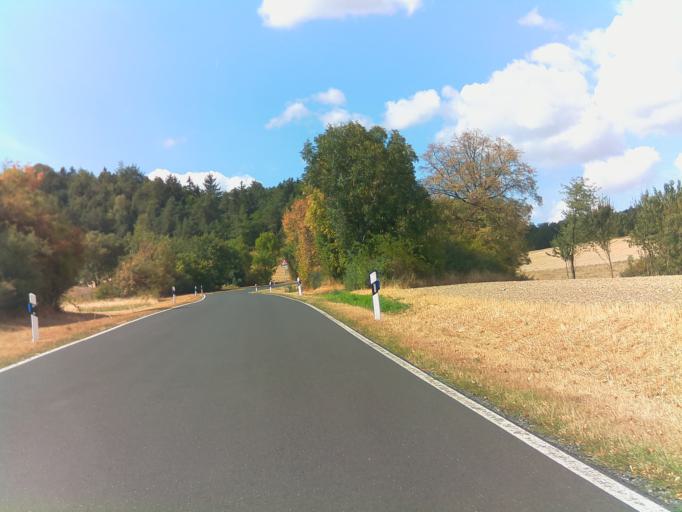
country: DE
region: Bavaria
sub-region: Regierungsbezirk Unterfranken
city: Oberelsbach
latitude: 50.4606
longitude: 10.1187
